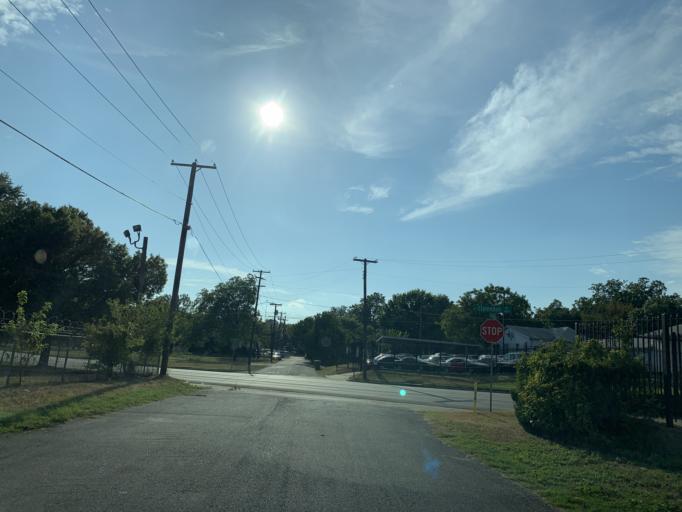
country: US
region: Texas
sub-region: Dallas County
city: Dallas
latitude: 32.7433
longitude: -96.8107
